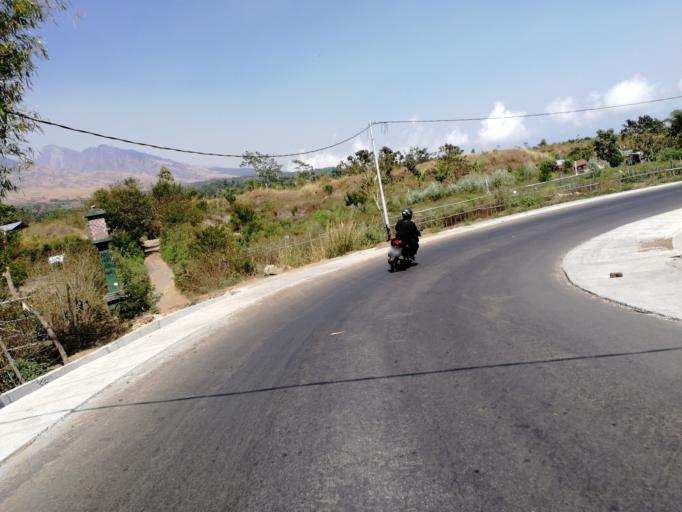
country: ID
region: West Nusa Tenggara
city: Sembalunlawang
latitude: -8.3577
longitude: 116.5140
